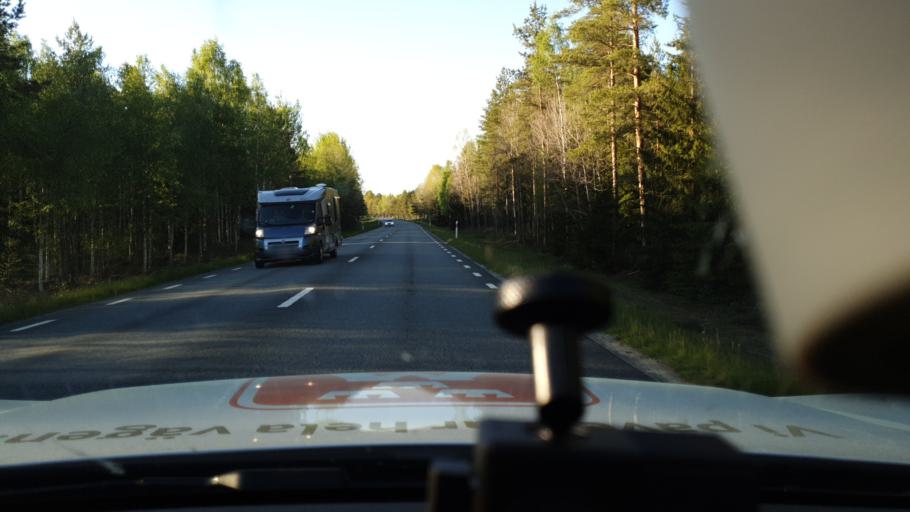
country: SE
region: Joenkoeping
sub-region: Eksjo Kommun
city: Eksjoe
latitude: 57.5922
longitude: 14.9691
